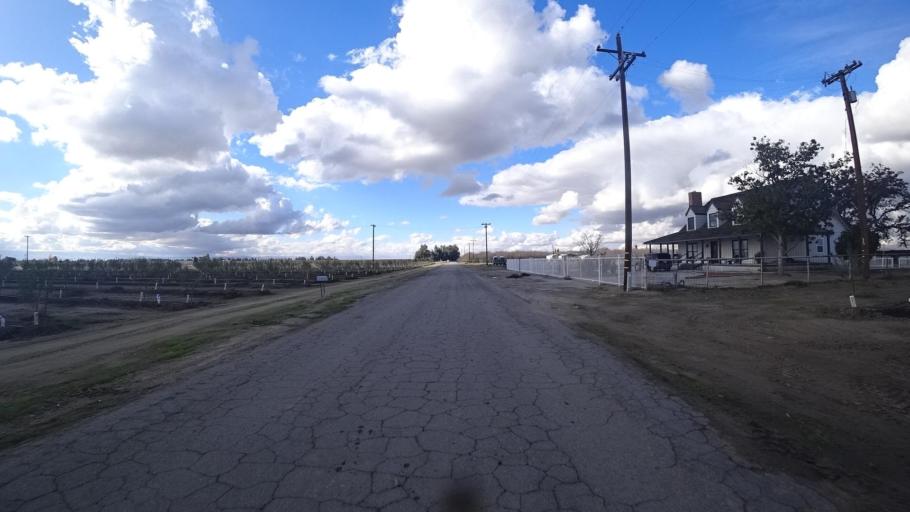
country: US
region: California
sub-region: Kern County
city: Greenfield
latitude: 35.2525
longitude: -119.0674
